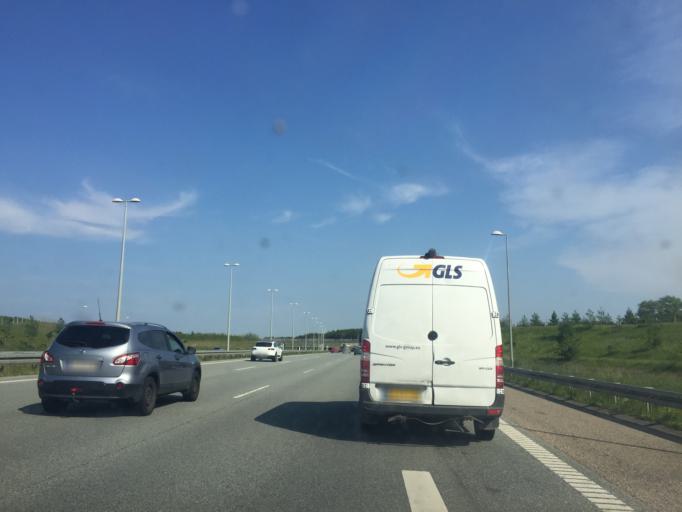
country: DK
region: Capital Region
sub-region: Glostrup Kommune
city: Glostrup
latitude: 55.6938
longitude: 12.3984
